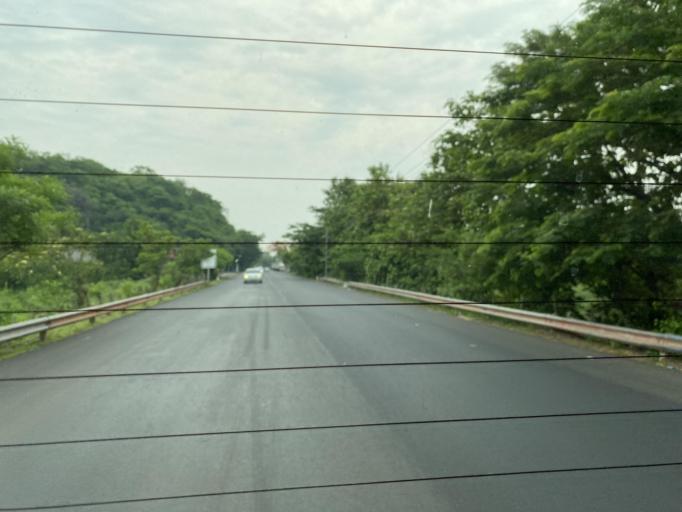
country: SV
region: San Miguel
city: Chirilagua
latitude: 13.3420
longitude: -88.1467
